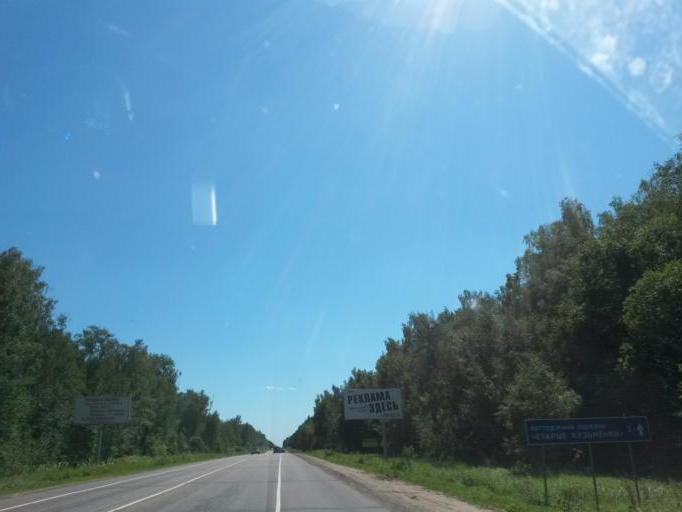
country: RU
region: Moskovskaya
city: Proletarskiy
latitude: 55.0608
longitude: 37.4351
